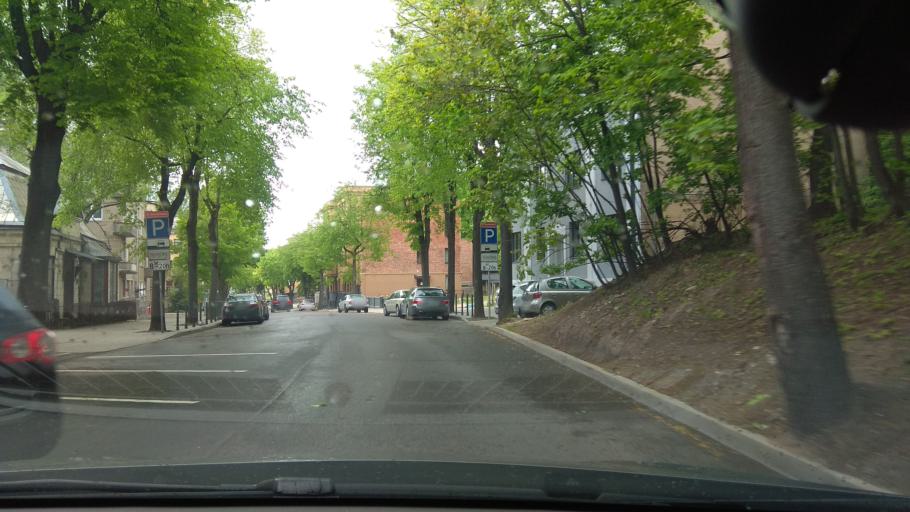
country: LT
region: Kauno apskritis
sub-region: Kaunas
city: Kaunas
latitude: 54.9003
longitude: 23.9208
